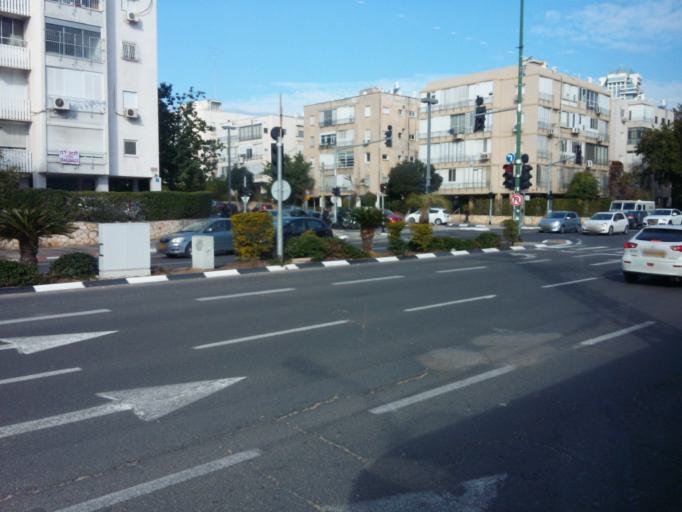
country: IL
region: Tel Aviv
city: Tel Aviv
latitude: 32.0853
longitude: 34.7951
